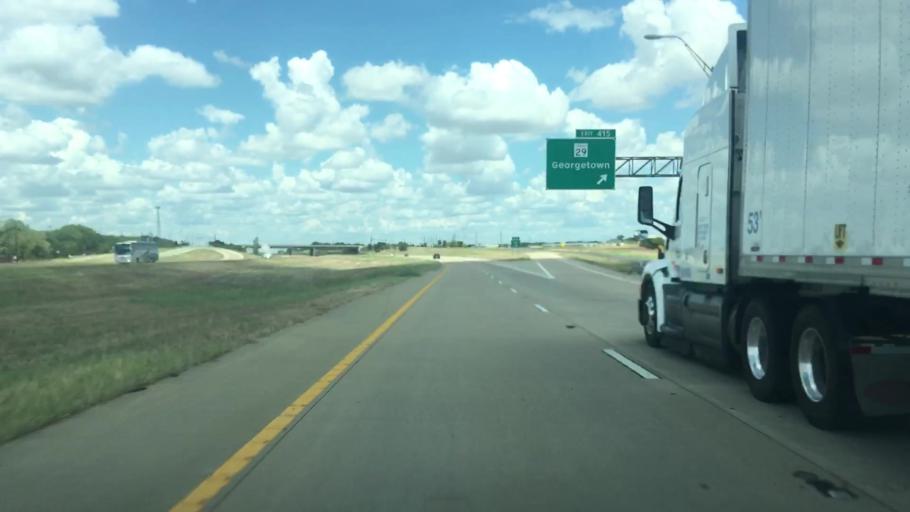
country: US
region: Texas
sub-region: Williamson County
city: Georgetown
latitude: 30.6355
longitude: -97.6281
